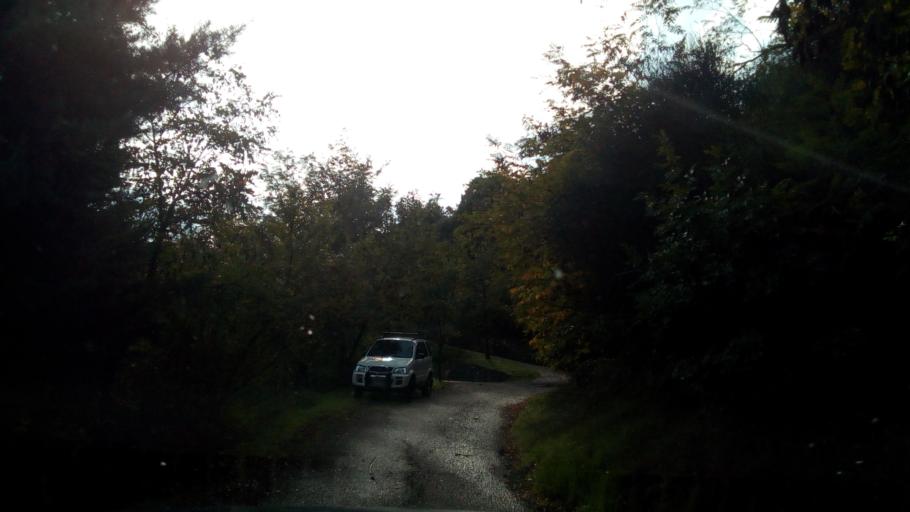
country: GR
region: Central Greece
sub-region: Nomos Fokidos
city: Lidoriki
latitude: 38.4890
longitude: 22.0538
